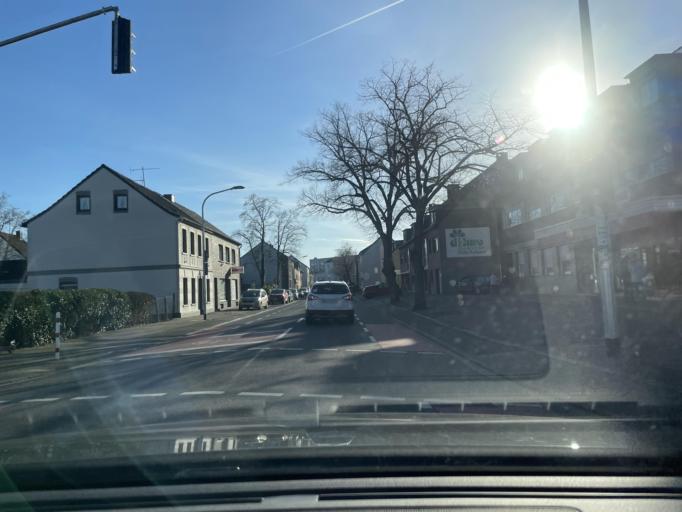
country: DE
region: North Rhine-Westphalia
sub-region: Regierungsbezirk Dusseldorf
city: Monchengladbach
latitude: 51.2193
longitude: 6.4699
